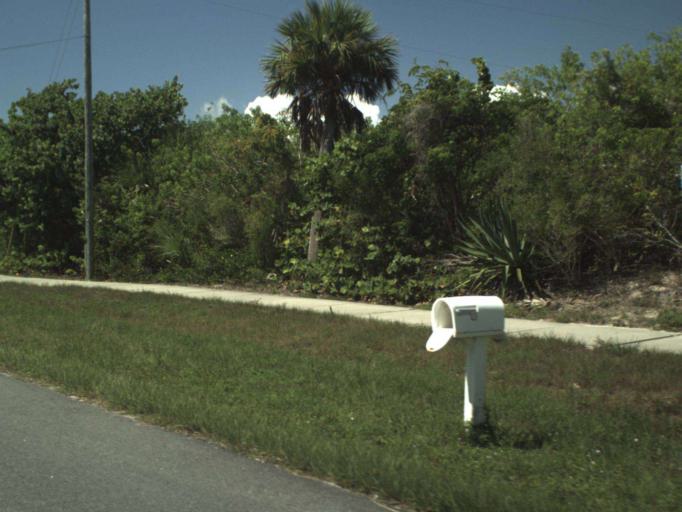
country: US
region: Florida
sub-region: Saint Lucie County
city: Fort Pierce
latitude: 27.5044
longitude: -80.3045
